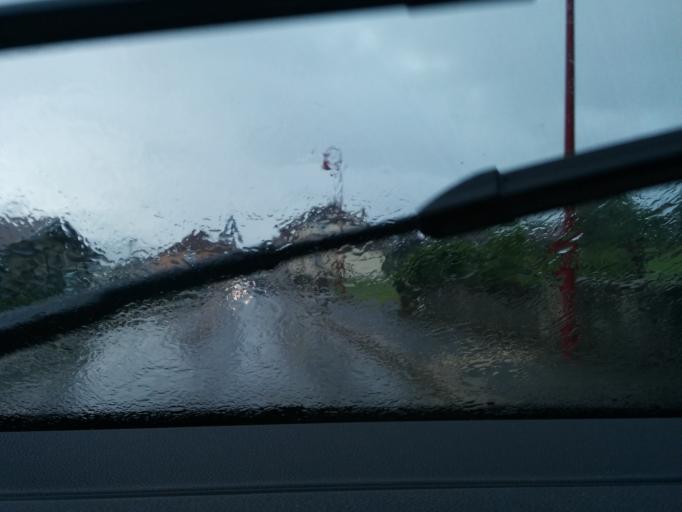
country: FR
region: Franche-Comte
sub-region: Departement du Jura
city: Saint-Lupicin
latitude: 46.4034
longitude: 5.7935
